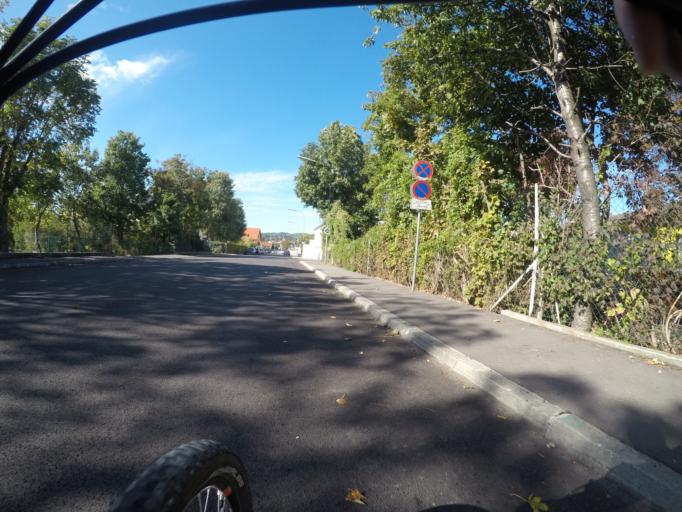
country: AT
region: Lower Austria
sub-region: Politischer Bezirk Modling
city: Brunn am Gebirge
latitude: 48.1077
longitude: 16.2982
